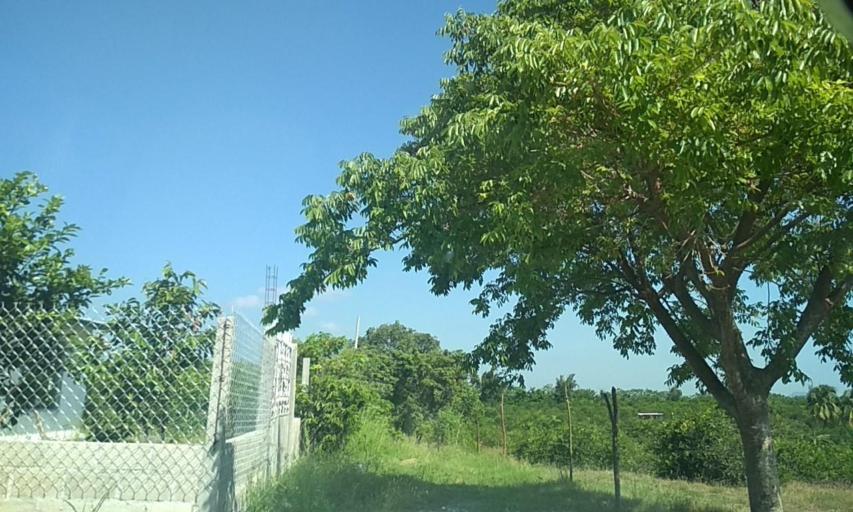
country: MX
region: Veracruz
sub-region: Martinez de la Torre
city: La Union Paso Largo
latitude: 20.1491
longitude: -96.9999
